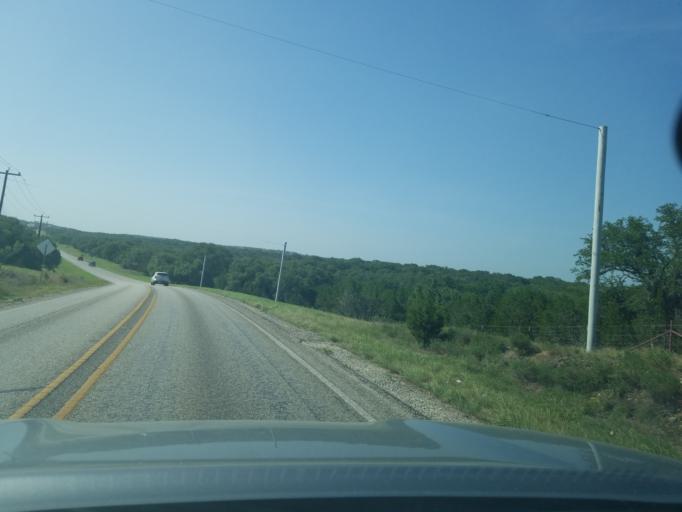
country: US
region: Texas
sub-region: Comal County
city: Garden Ridge
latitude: 29.6752
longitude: -98.3192
